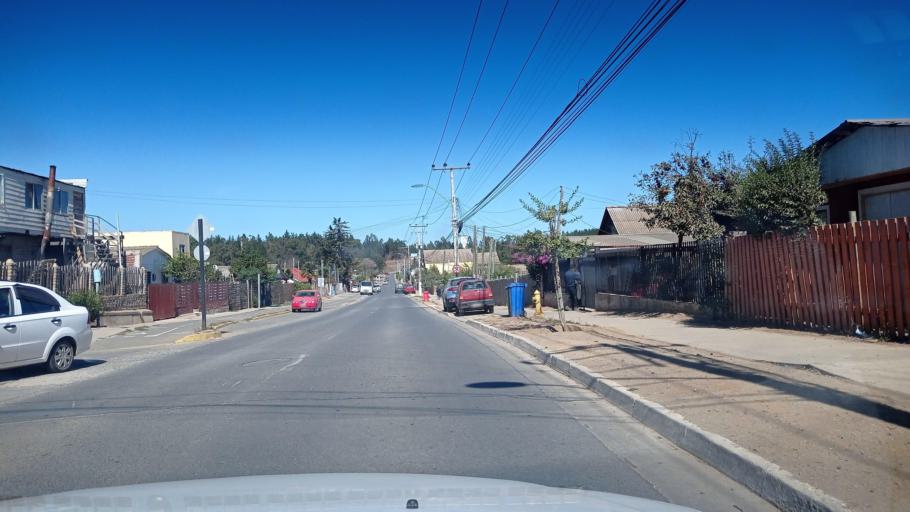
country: CL
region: O'Higgins
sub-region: Provincia de Colchagua
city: Santa Cruz
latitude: -34.4043
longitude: -71.9958
